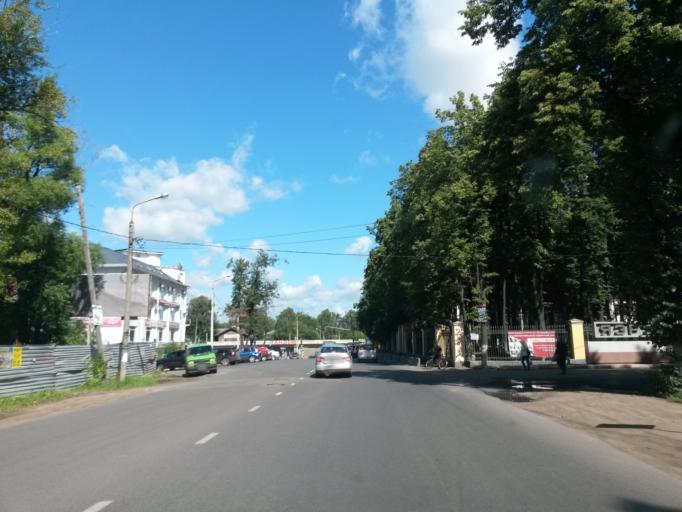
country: RU
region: Jaroslavl
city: Yaroslavl
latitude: 57.6003
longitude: 39.8779
